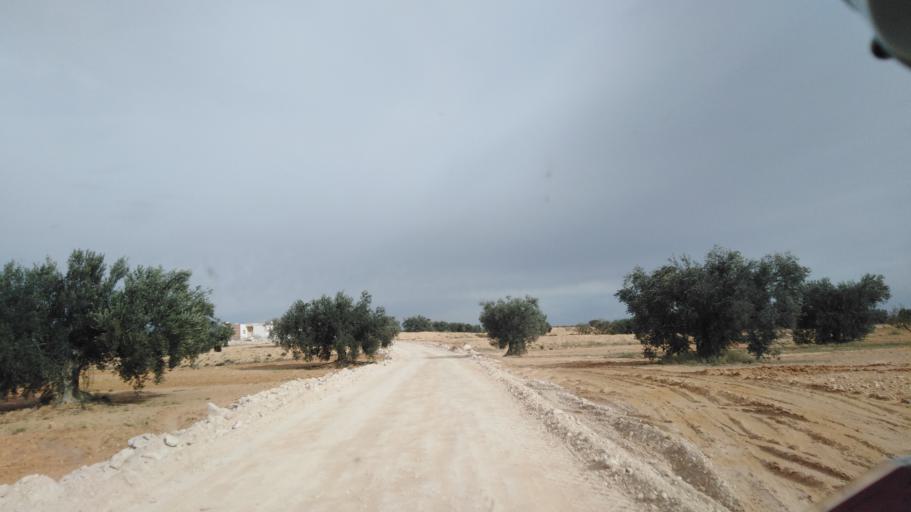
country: TN
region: Safaqis
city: Bi'r `Ali Bin Khalifah
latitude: 34.8126
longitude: 10.3071
